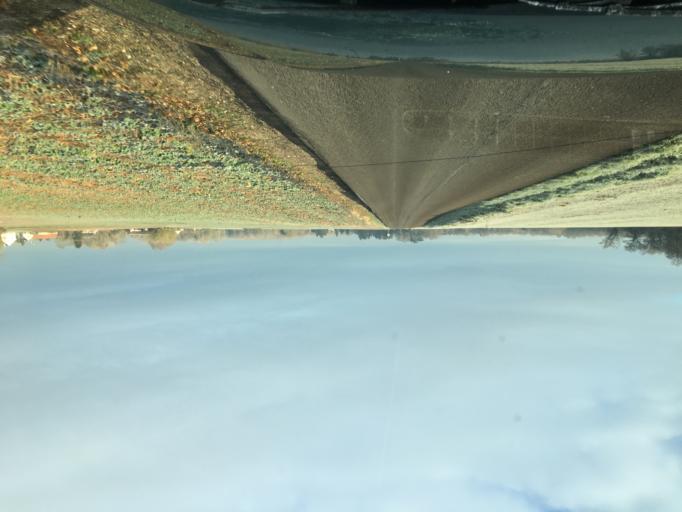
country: FR
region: Centre
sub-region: Departement du Loiret
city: Clery-Saint-Andre
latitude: 47.8180
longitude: 1.8005
